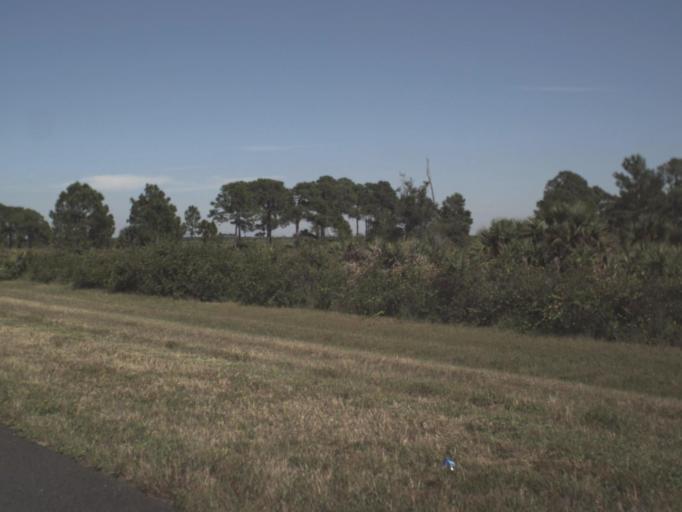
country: US
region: Florida
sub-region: Highlands County
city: Placid Lakes
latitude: 27.1042
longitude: -81.3323
